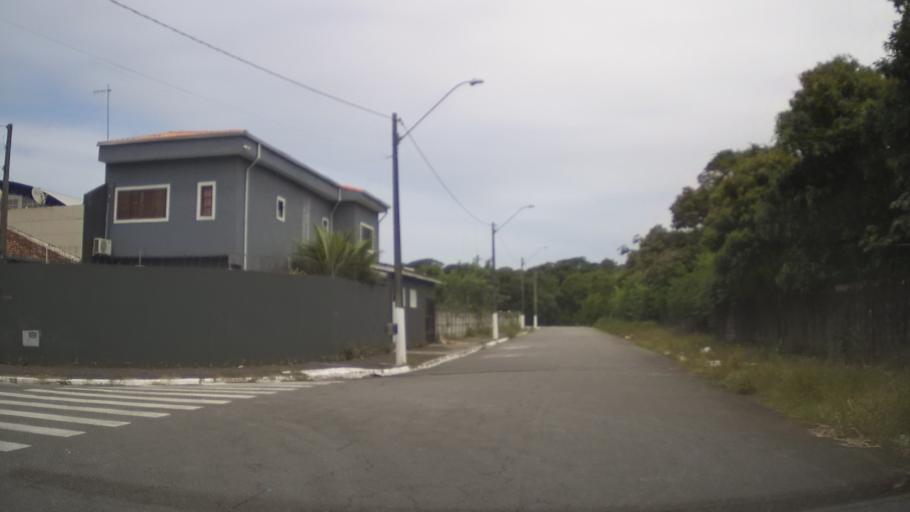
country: BR
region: Sao Paulo
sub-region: Praia Grande
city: Praia Grande
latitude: -24.0268
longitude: -46.5037
